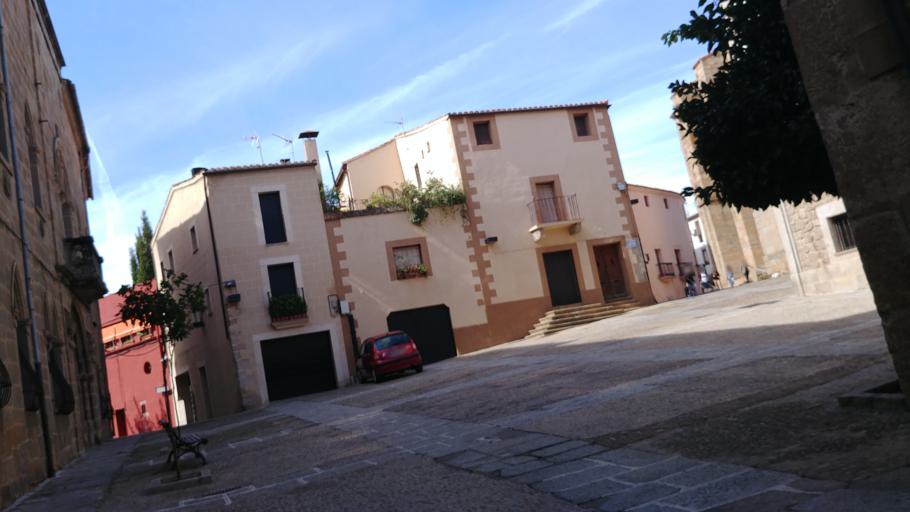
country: ES
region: Extremadura
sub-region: Provincia de Caceres
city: Plasencia
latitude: 40.0286
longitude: -6.0923
